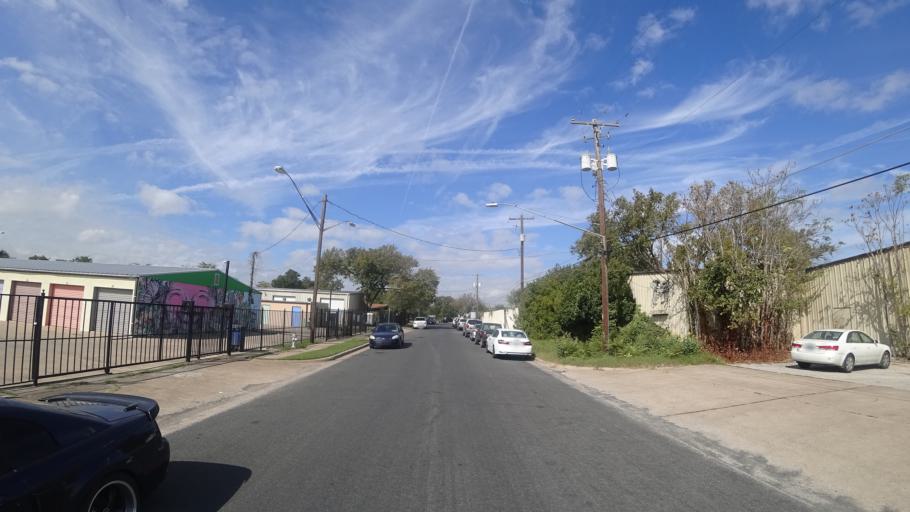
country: US
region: Texas
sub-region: Travis County
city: Austin
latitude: 30.2534
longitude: -97.7048
